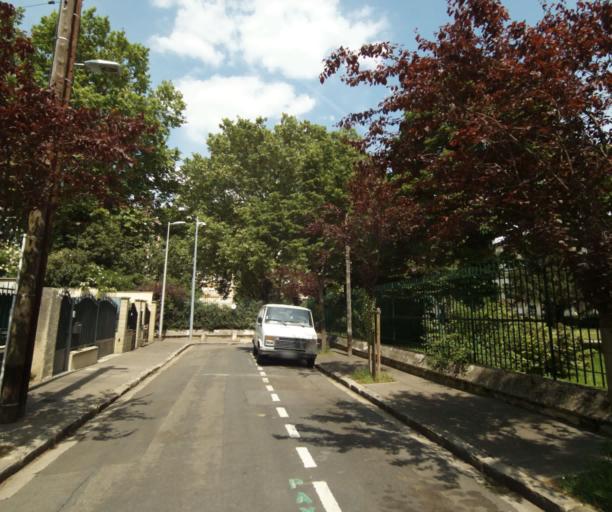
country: FR
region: Ile-de-France
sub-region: Departement des Hauts-de-Seine
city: Colombes
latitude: 48.9268
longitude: 2.2505
